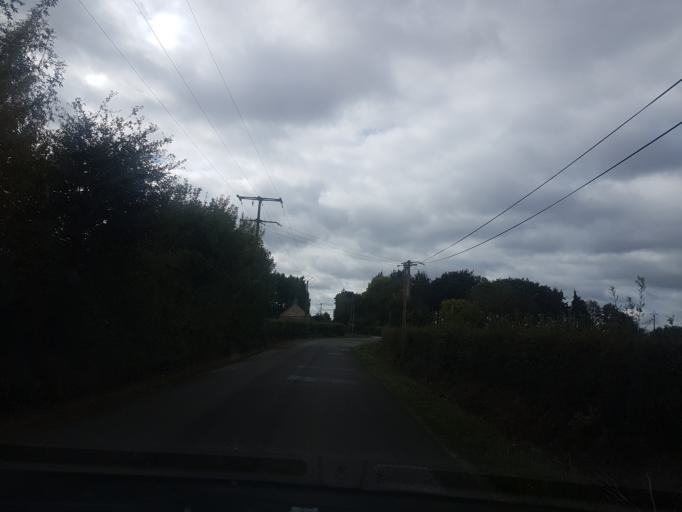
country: FR
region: Pays de la Loire
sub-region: Departement de la Loire-Atlantique
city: Ligne
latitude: 47.4059
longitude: -1.3852
